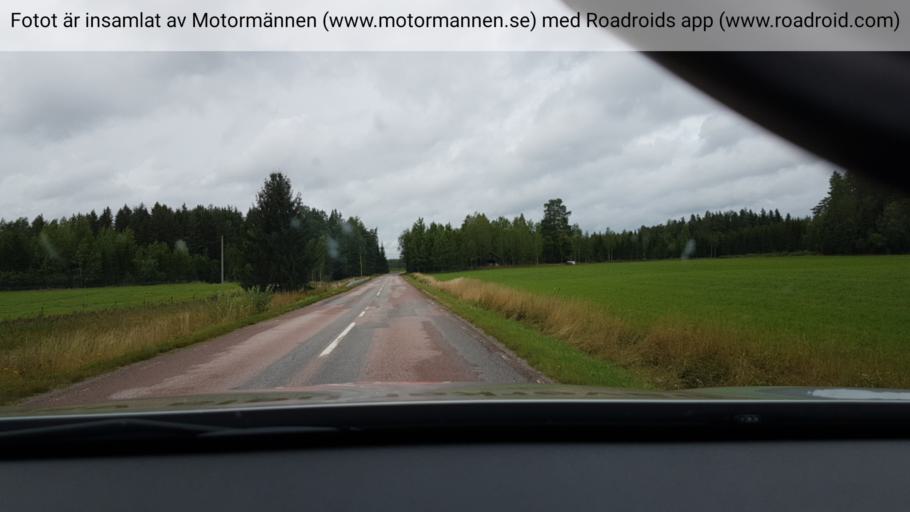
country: SE
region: Uppsala
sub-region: Heby Kommun
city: Tarnsjo
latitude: 60.1783
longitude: 17.0335
